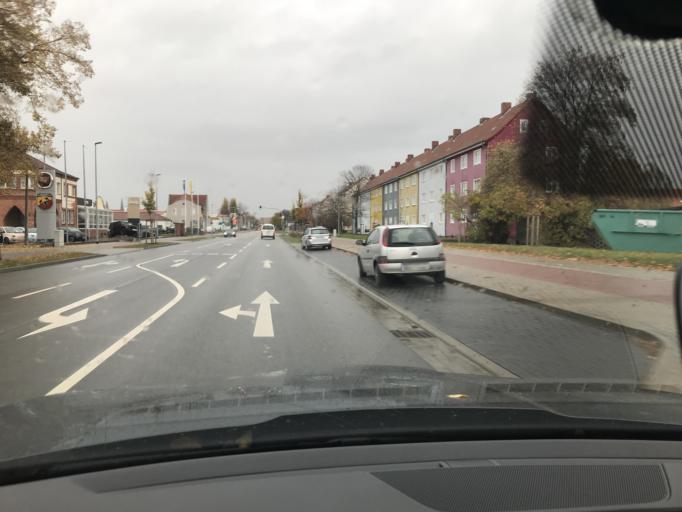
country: DE
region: Saxony-Anhalt
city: Halberstadt
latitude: 51.8864
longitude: 11.0676
